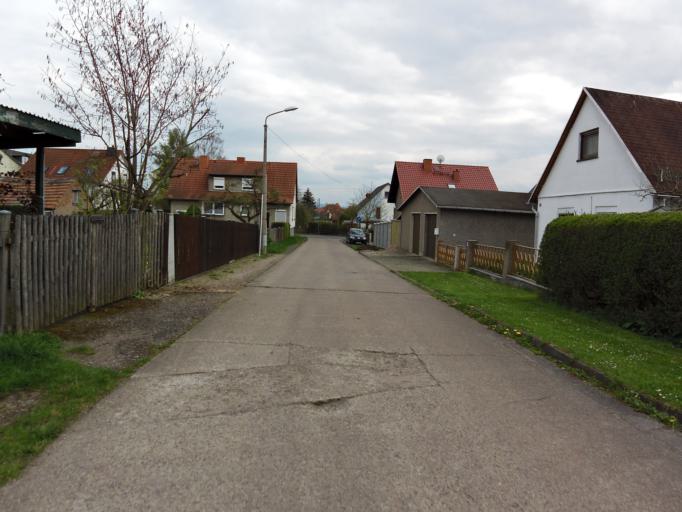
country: DE
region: Thuringia
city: Gotha
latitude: 50.9337
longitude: 10.6722
